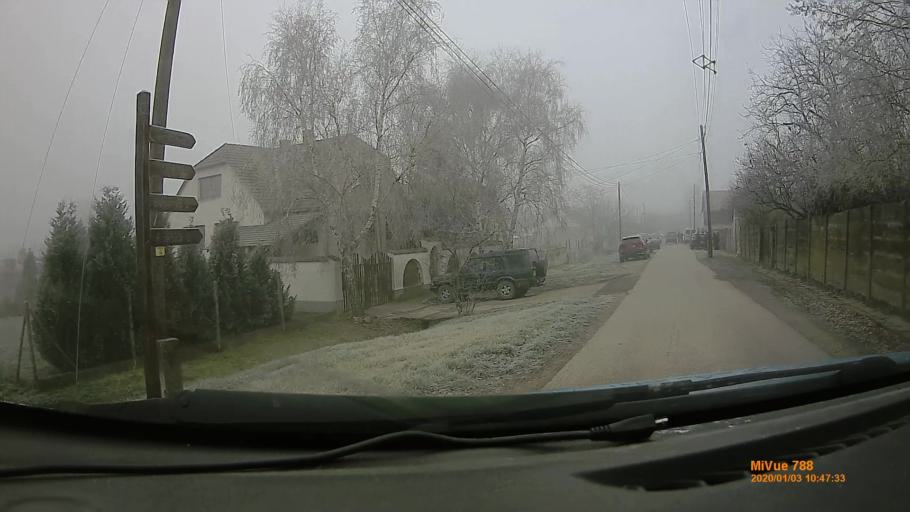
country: HU
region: Tolna
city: Bataszek
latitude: 46.2044
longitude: 18.7338
